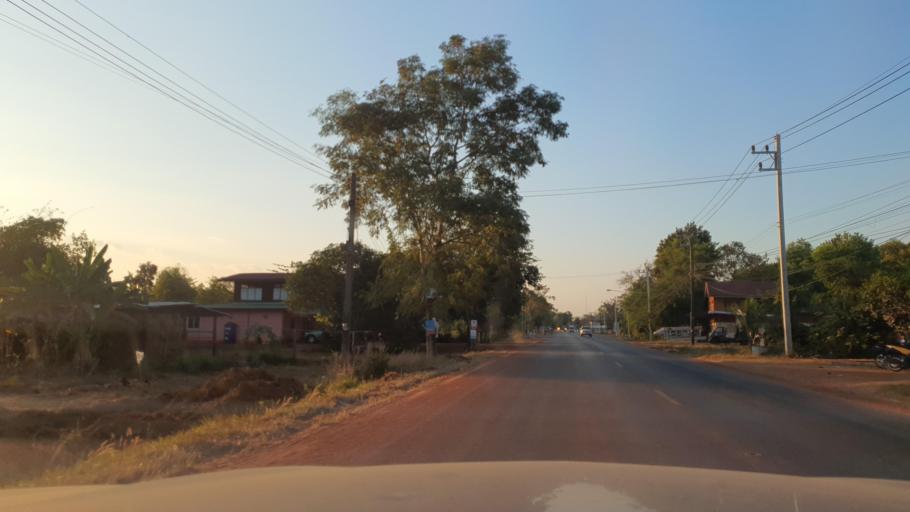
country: TH
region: Nakhon Phanom
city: Si Songkhram
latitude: 17.7633
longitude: 104.2815
